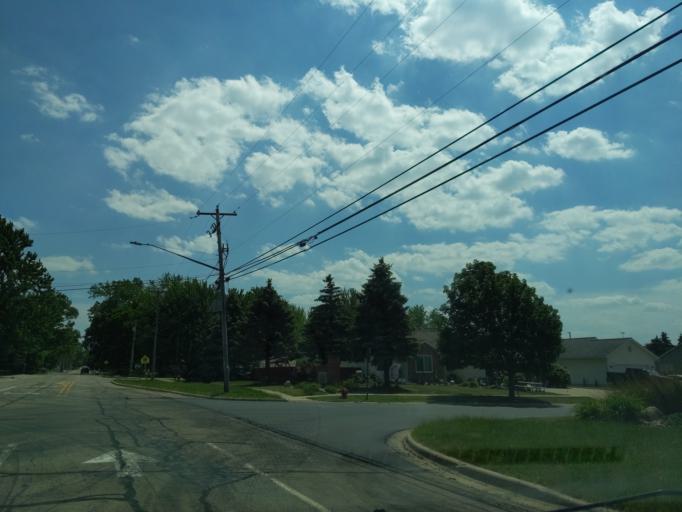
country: US
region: Michigan
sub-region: Clinton County
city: Saint Johns
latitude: 43.0132
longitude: -84.5627
